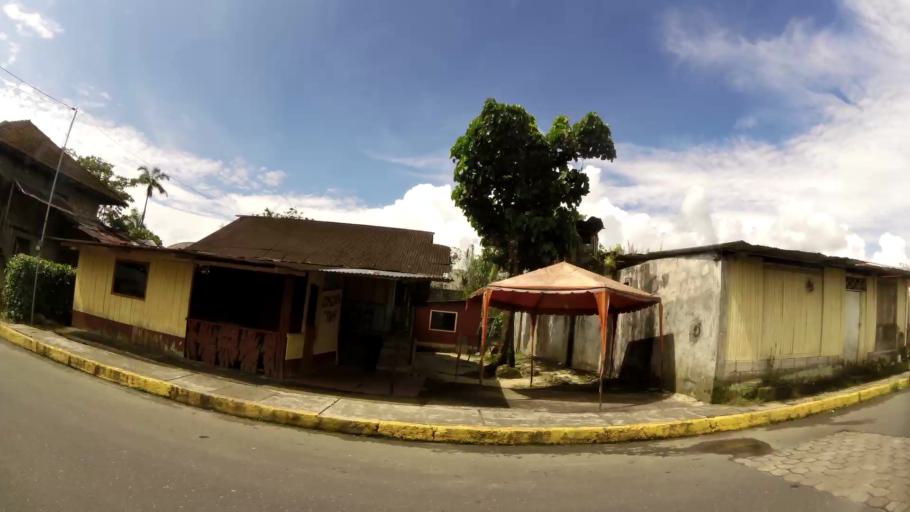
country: EC
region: Pastaza
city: Puyo
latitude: -1.4608
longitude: -78.1130
